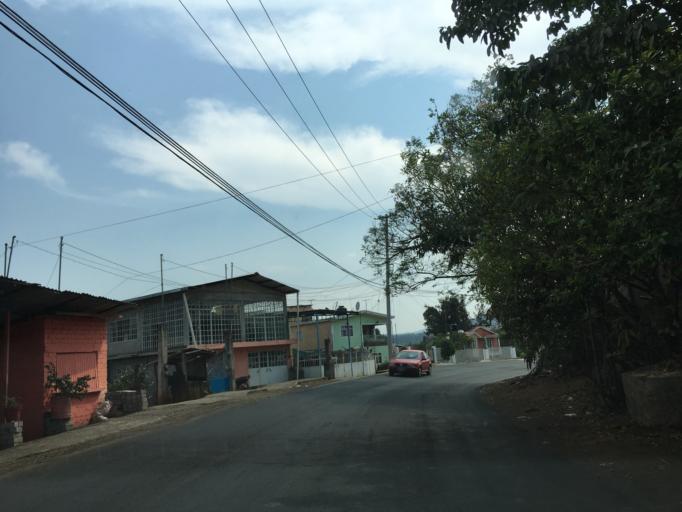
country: MX
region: Michoacan
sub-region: Ziracuaretiro
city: Patuan
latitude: 19.4172
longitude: -101.9151
